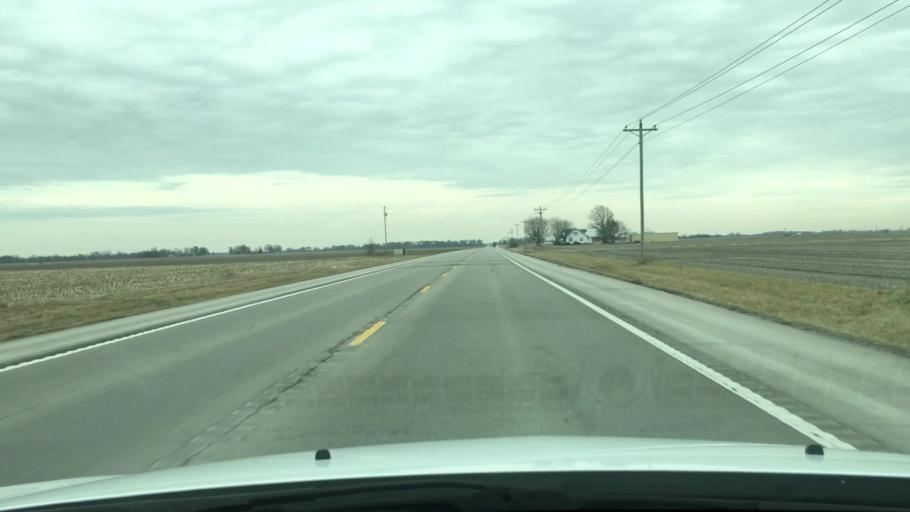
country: US
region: Missouri
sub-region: Audrain County
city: Mexico
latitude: 39.1639
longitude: -91.7831
